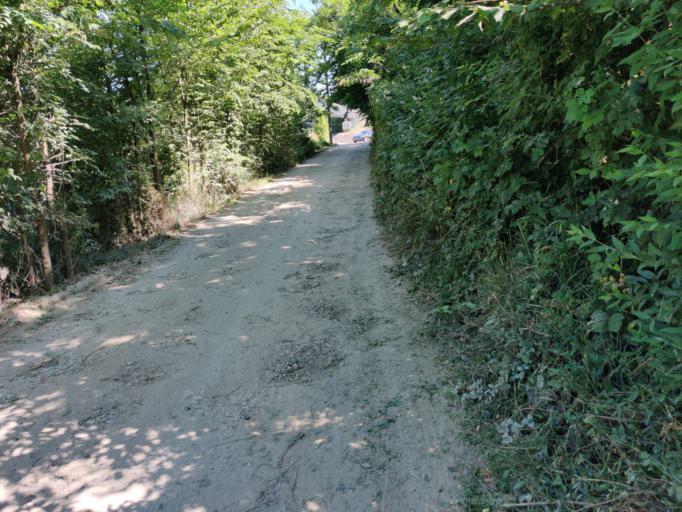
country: HU
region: Hajdu-Bihar
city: Balmazujvaros
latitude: 47.6032
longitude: 21.3791
